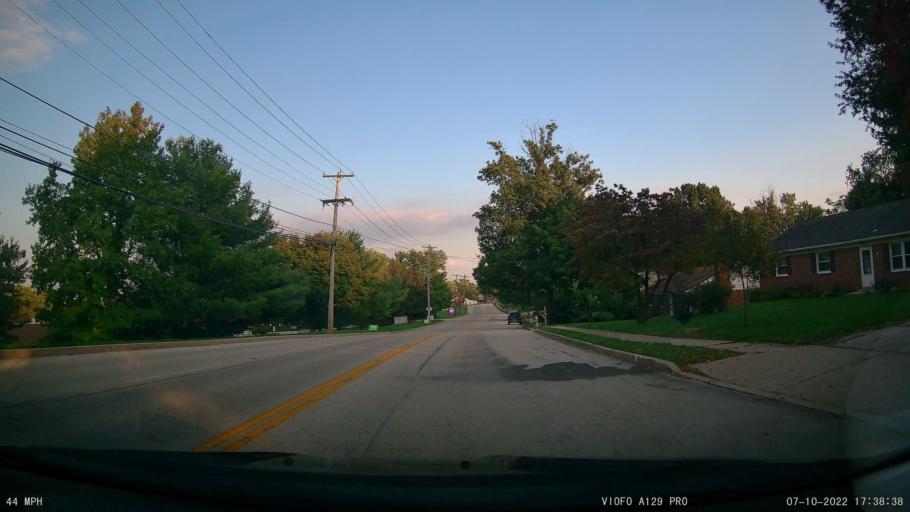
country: US
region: Pennsylvania
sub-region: Montgomery County
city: King of Prussia
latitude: 40.1035
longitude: -75.3947
